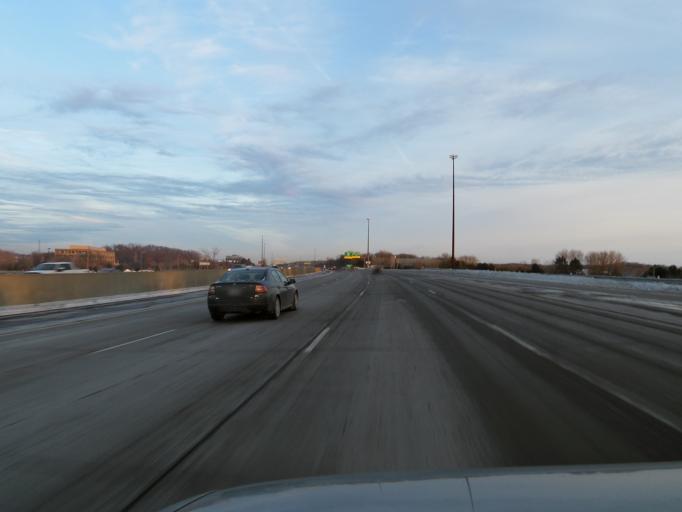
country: US
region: Minnesota
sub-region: Hennepin County
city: Eden Prairie
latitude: 44.8593
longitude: -93.4161
